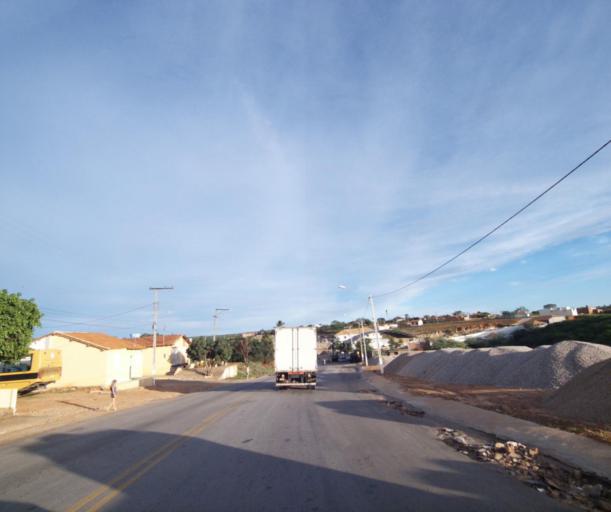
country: BR
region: Bahia
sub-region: Cacule
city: Cacule
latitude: -14.2066
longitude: -42.1096
